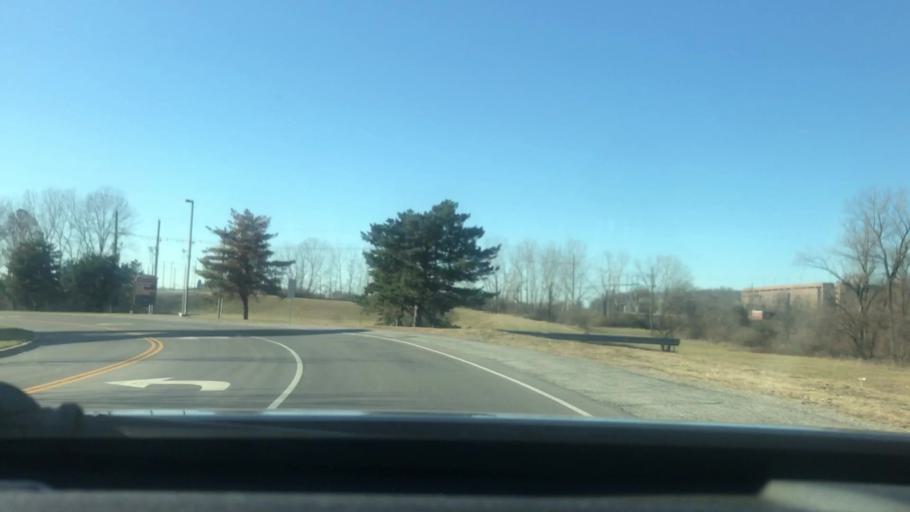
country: US
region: Missouri
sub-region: Clay County
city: North Kansas City
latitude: 39.1446
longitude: -94.5450
